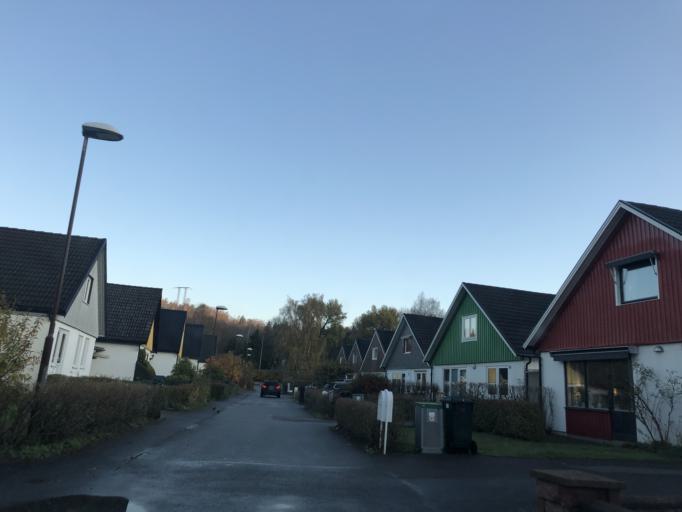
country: SE
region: Vaestra Goetaland
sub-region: Goteborg
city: Hammarkullen
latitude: 57.7889
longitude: 12.0303
